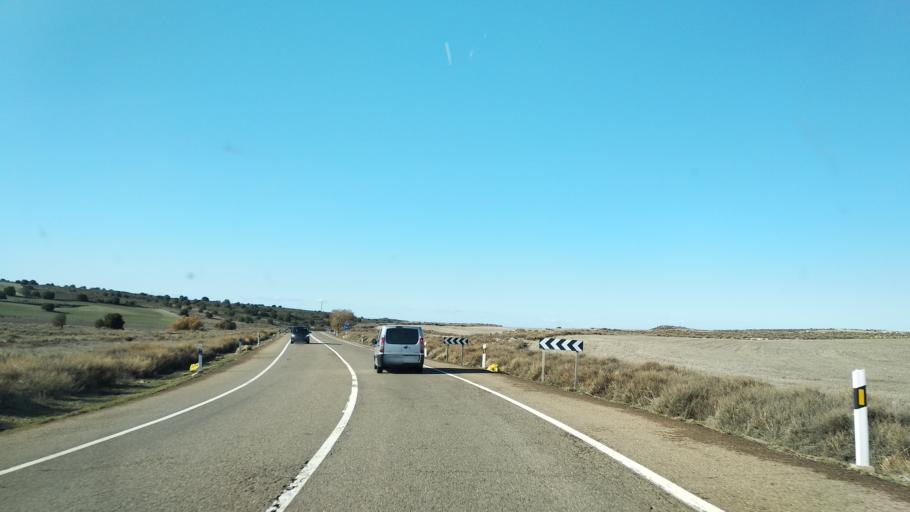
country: ES
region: Aragon
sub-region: Provincia de Zaragoza
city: Bujaraloz
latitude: 41.4936
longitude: -0.2342
